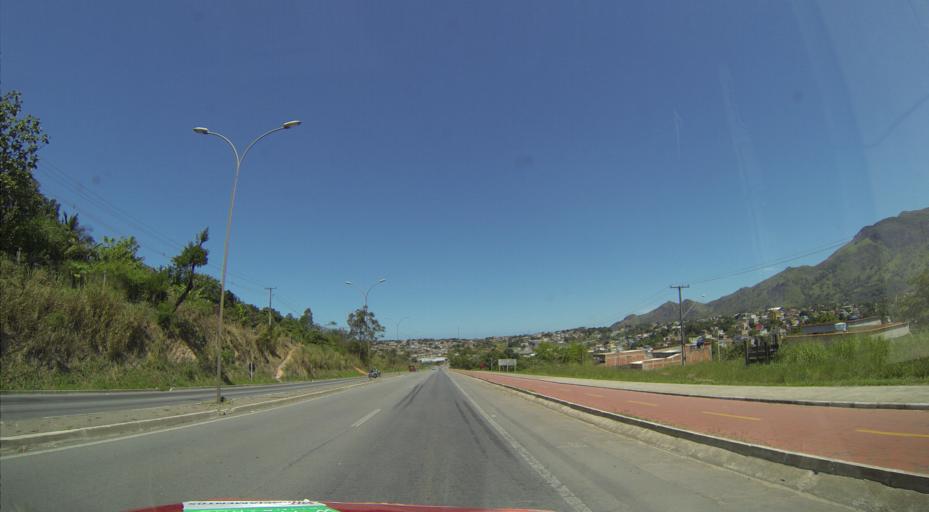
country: BR
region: Espirito Santo
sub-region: Serra
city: Serra
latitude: -20.1294
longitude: -40.2977
